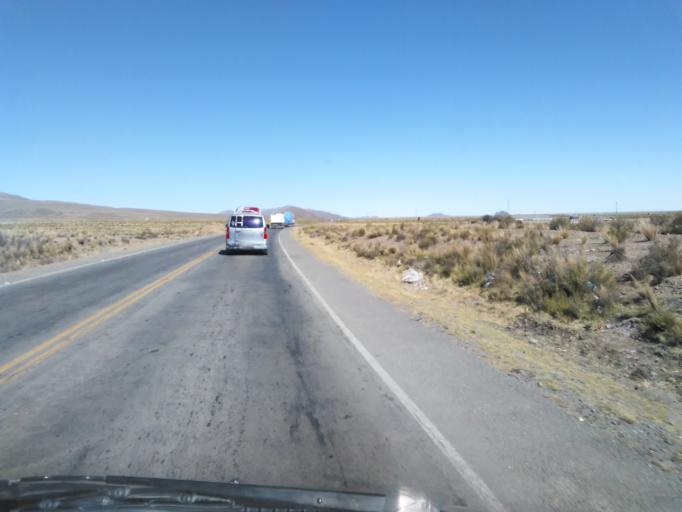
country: BO
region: Oruro
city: Machacamarca
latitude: -18.0595
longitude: -67.0060
